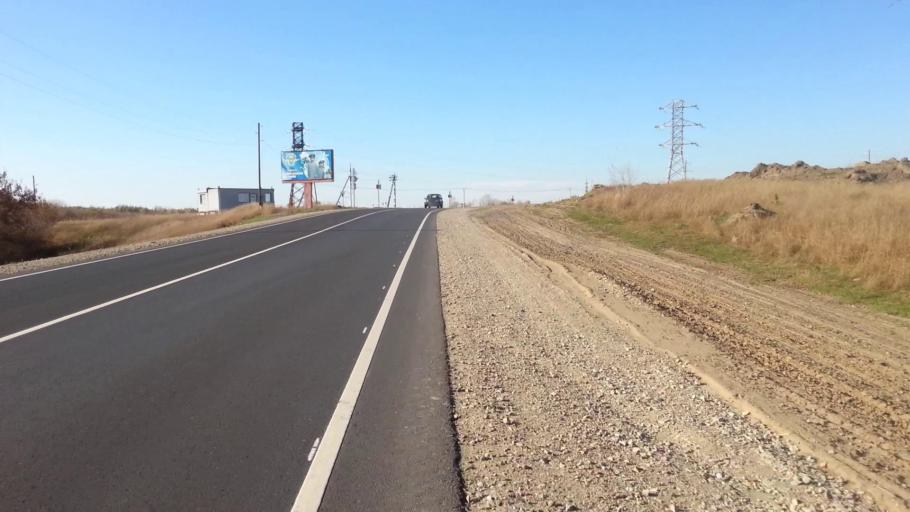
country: RU
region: Altai Krai
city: Sannikovo
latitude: 53.3287
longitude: 83.9401
